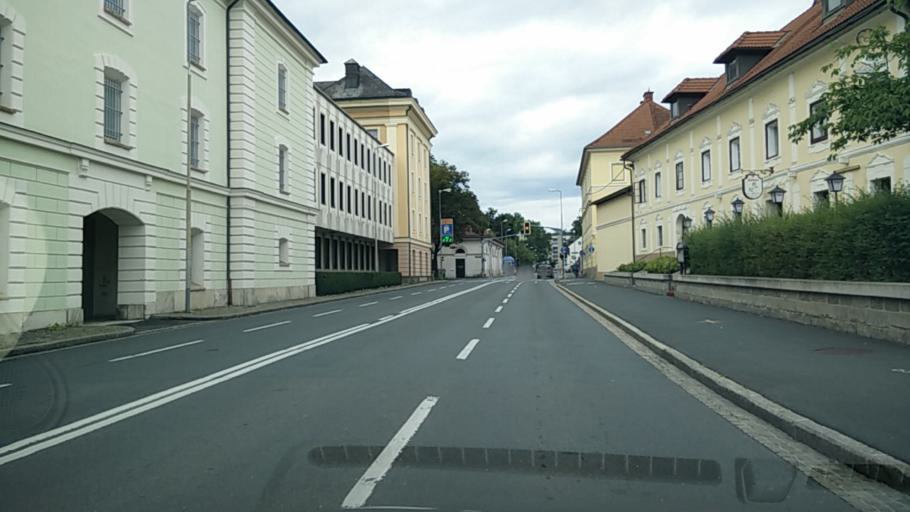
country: AT
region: Carinthia
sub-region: Klagenfurt am Woerthersee
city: Klagenfurt am Woerthersee
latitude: 46.6280
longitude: 14.3077
